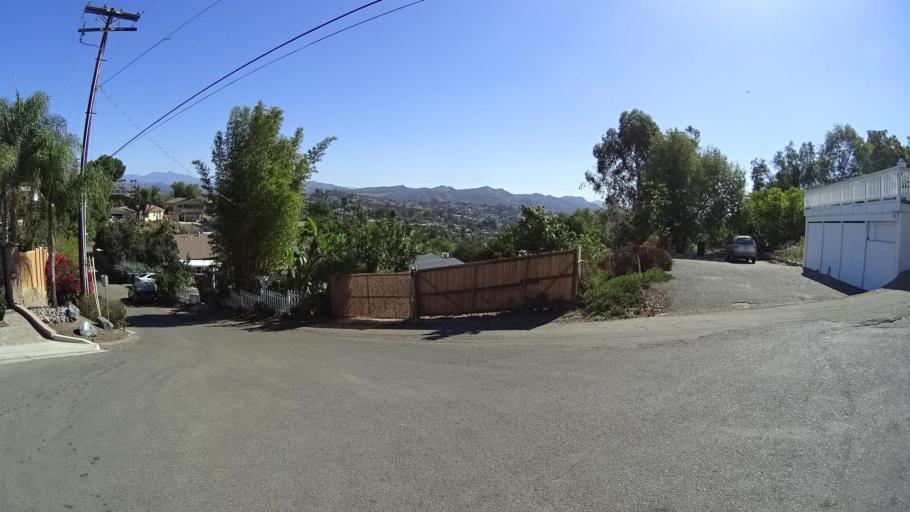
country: US
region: California
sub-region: San Diego County
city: Winter Gardens
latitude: 32.8311
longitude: -116.9402
